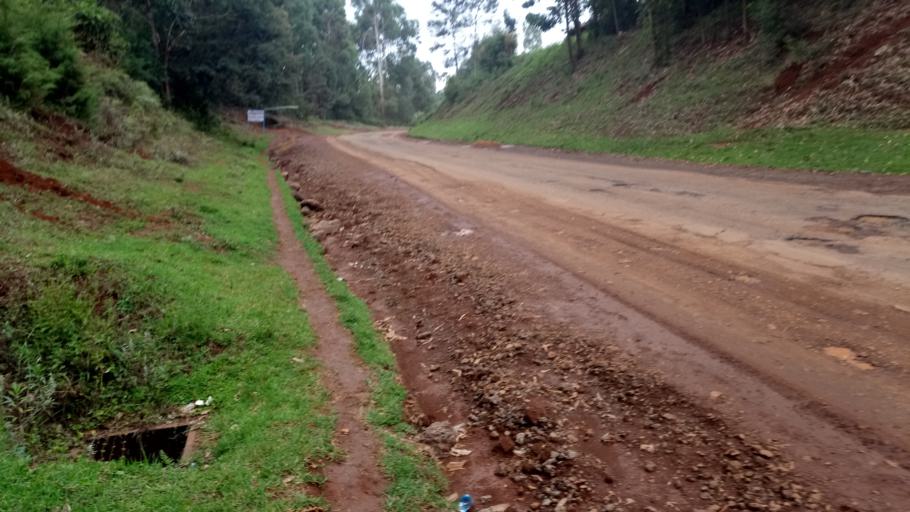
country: KE
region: Kirinyaga
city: Keruguya
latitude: -0.4235
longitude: 37.1591
